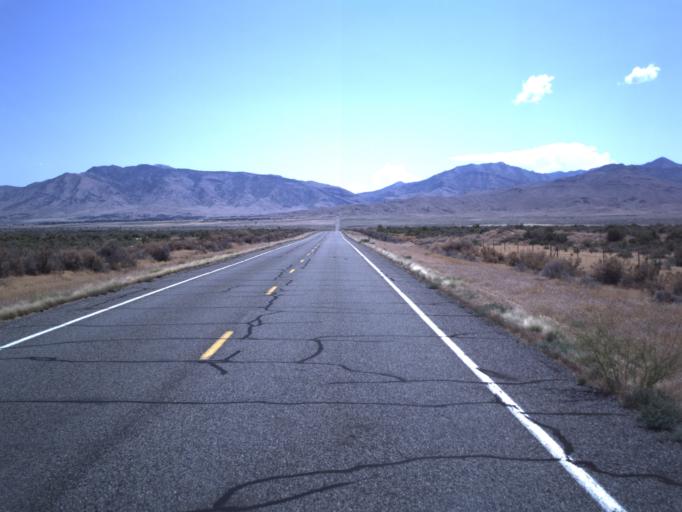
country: US
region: Utah
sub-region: Millard County
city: Delta
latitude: 39.3539
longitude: -112.4405
